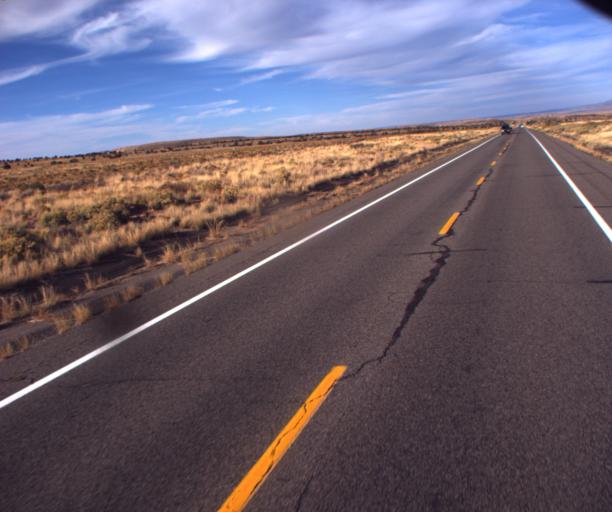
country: US
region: Colorado
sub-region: Montezuma County
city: Towaoc
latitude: 36.9622
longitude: -109.0657
